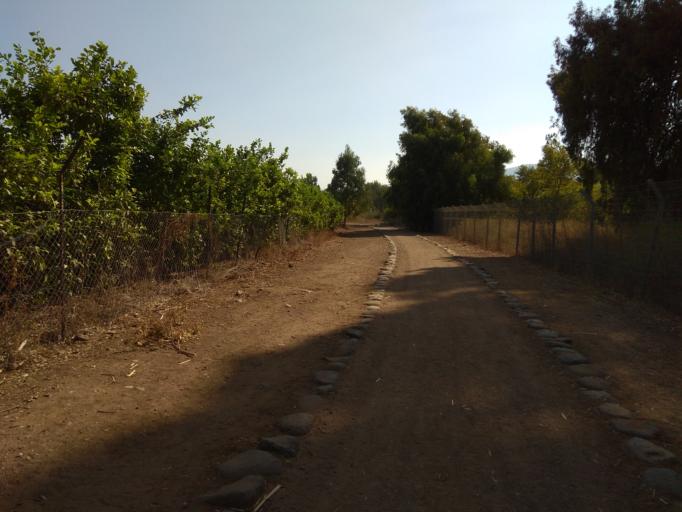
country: IL
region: Northern District
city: Qiryat Shemona
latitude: 33.2265
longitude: 35.6167
